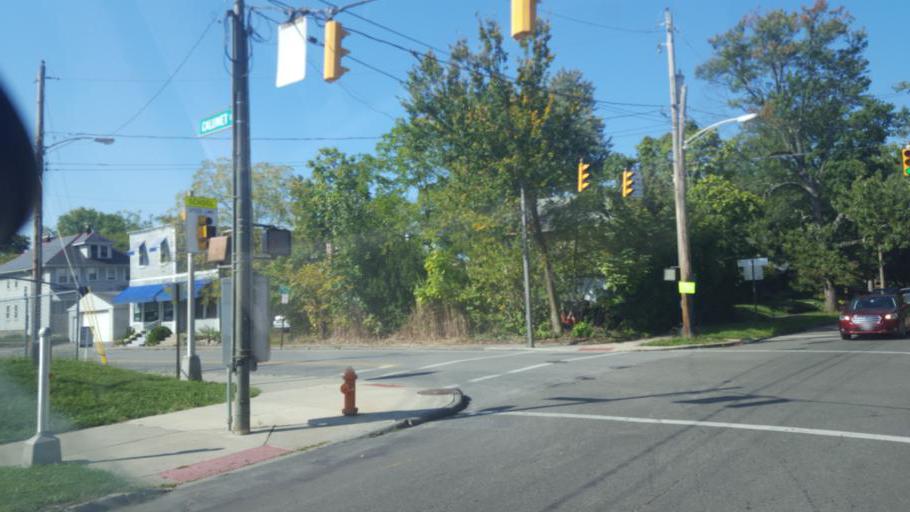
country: US
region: Ohio
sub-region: Franklin County
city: Grandview Heights
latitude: 40.0247
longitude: -83.0073
